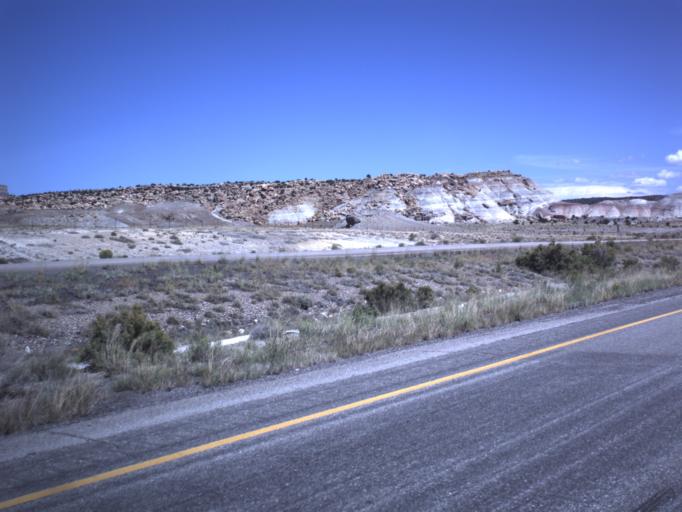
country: US
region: Utah
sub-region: Emery County
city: Ferron
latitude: 38.8160
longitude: -111.1850
